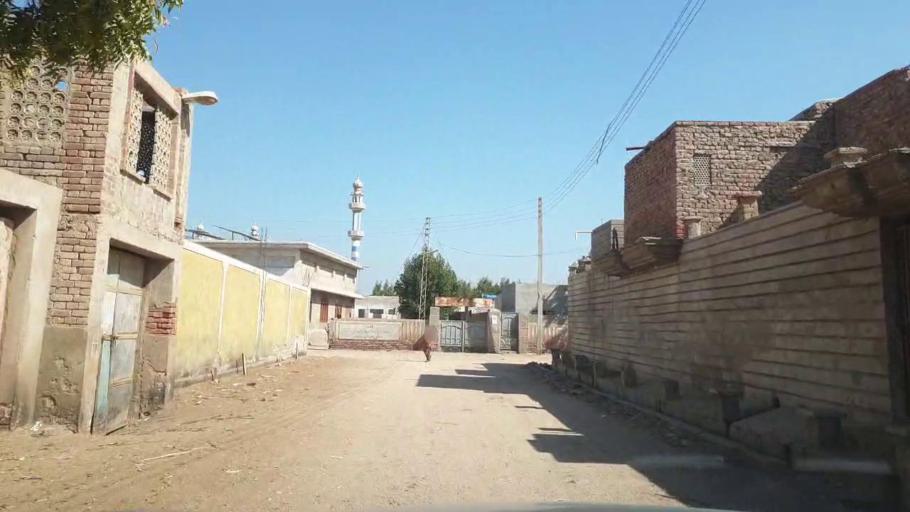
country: PK
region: Sindh
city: Tando Adam
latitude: 25.6512
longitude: 68.6981
